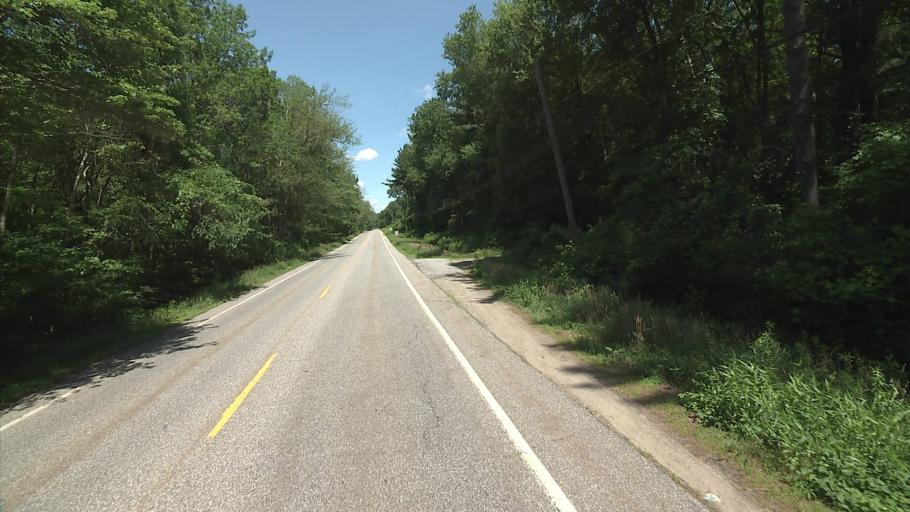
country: US
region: Connecticut
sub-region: New London County
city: Preston City
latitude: 41.4711
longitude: -71.9035
